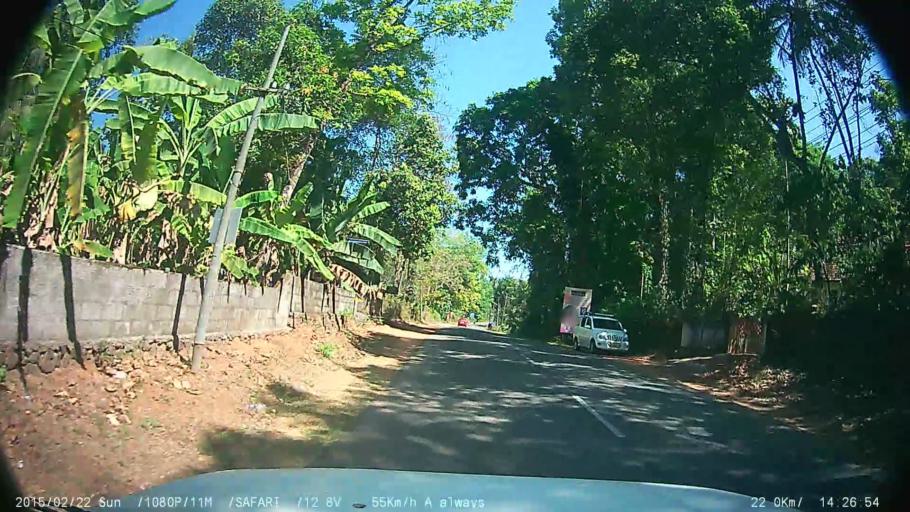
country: IN
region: Kerala
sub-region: Kottayam
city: Erattupetta
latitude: 9.5653
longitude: 76.7302
